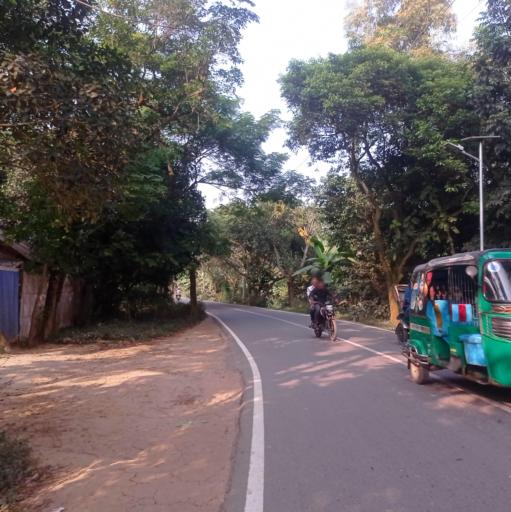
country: BD
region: Dhaka
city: Bhairab Bazar
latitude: 24.0849
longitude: 90.8499
